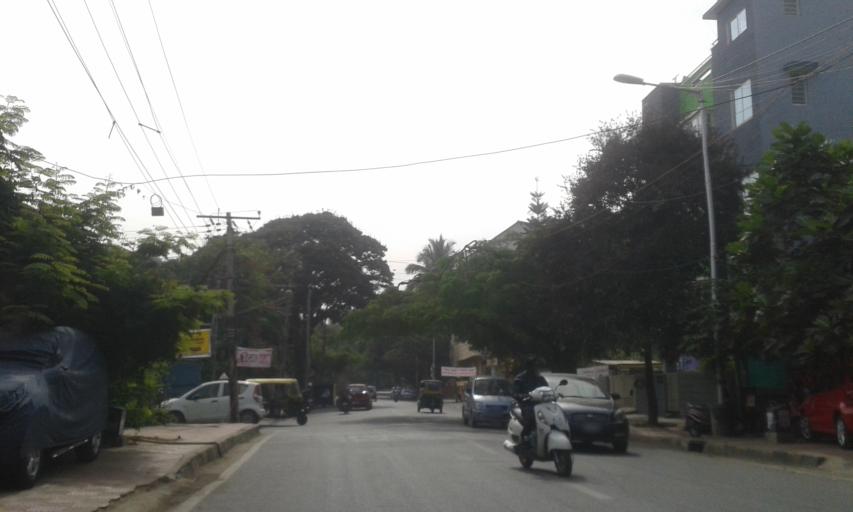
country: IN
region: Karnataka
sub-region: Bangalore Urban
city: Bangalore
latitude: 12.9332
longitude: 77.6274
